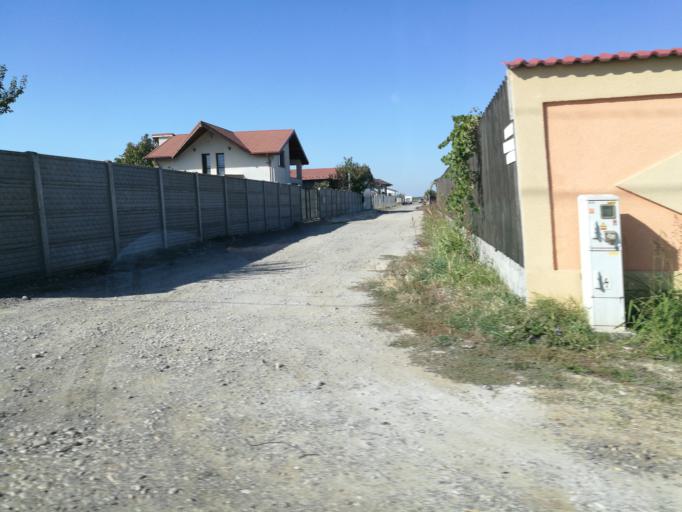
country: RO
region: Giurgiu
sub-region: Comuna Joita
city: Bacu
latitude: 44.4698
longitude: 25.8855
